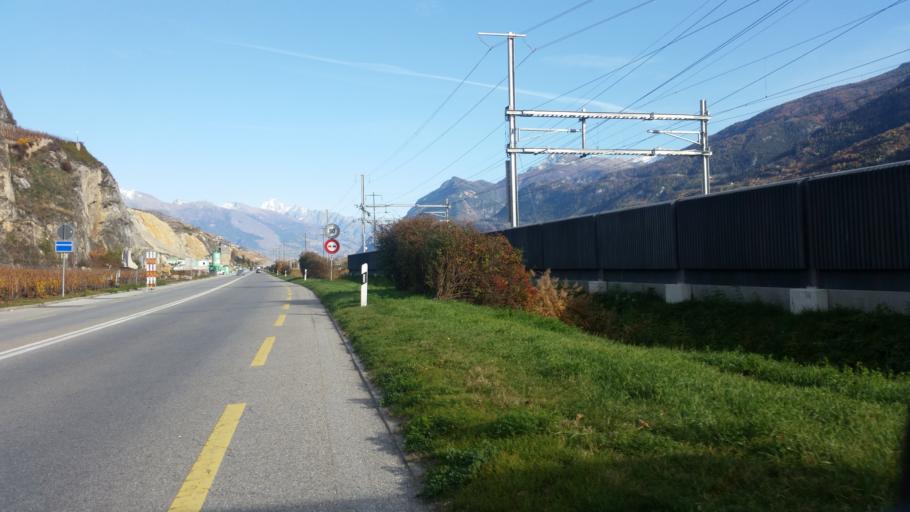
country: CH
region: Valais
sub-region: Sion District
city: Saint-Leonard
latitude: 46.2548
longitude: 7.4290
